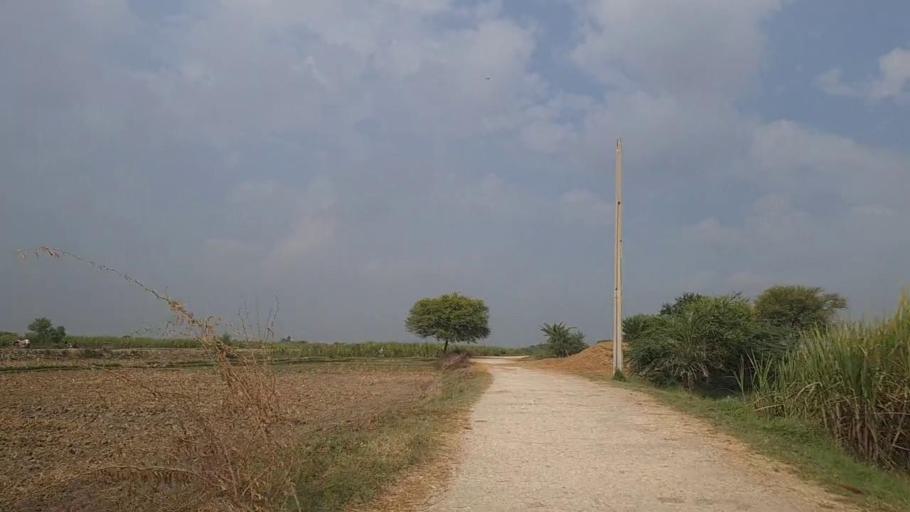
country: PK
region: Sindh
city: Daro Mehar
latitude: 24.6915
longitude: 68.1264
